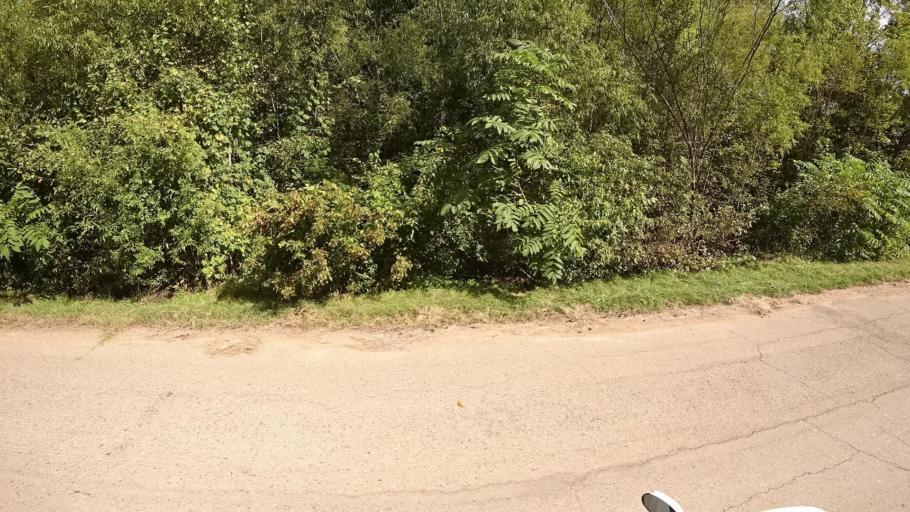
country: RU
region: Primorskiy
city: Yakovlevka
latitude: 44.7073
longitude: 133.6397
